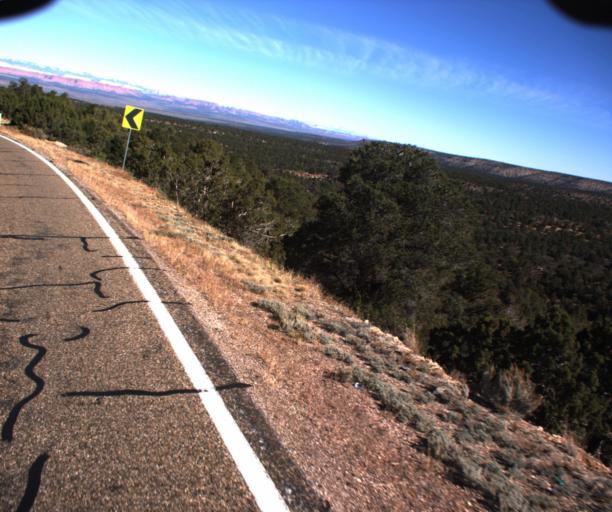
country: US
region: Arizona
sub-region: Coconino County
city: Fredonia
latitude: 36.8478
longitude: -112.2538
